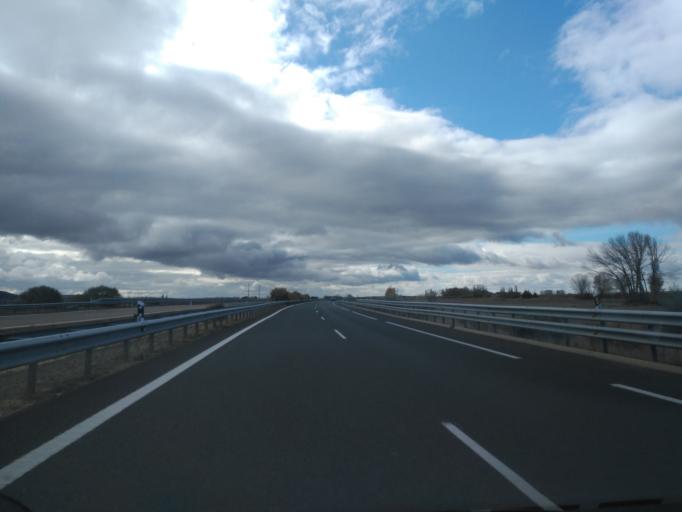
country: ES
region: Castille and Leon
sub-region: Provincia de Palencia
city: Pina de Campos
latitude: 42.2266
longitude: -4.4321
